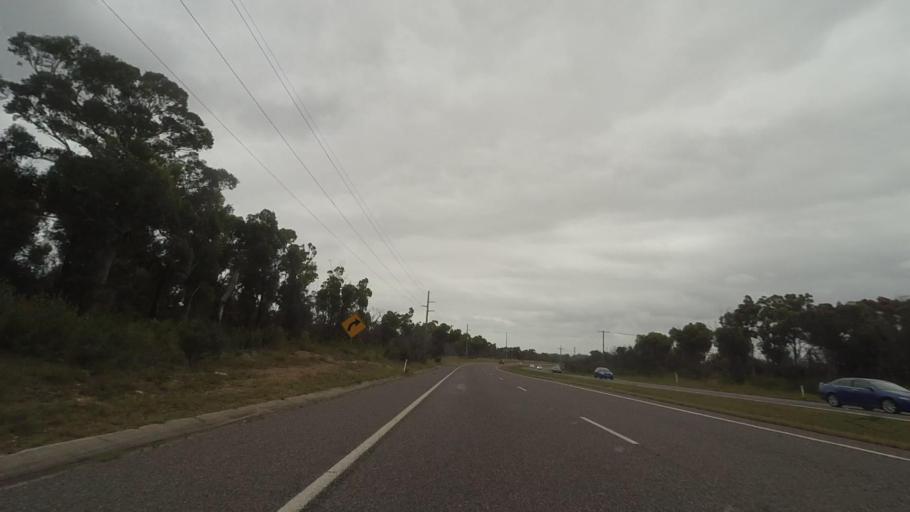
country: AU
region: New South Wales
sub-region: Wyong Shire
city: Kingfisher Shores
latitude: -33.1833
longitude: 151.5918
